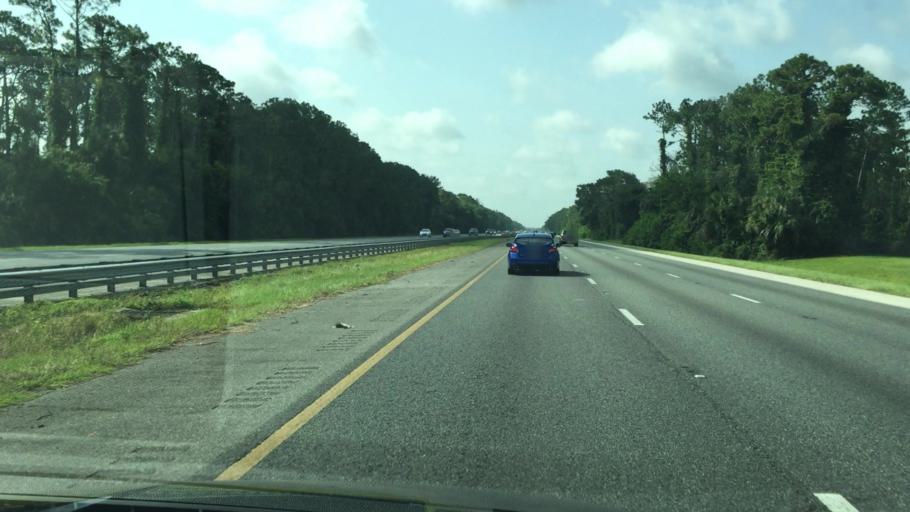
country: US
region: Florida
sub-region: Volusia County
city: Ormond-by-the-Sea
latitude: 29.3795
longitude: -81.1448
